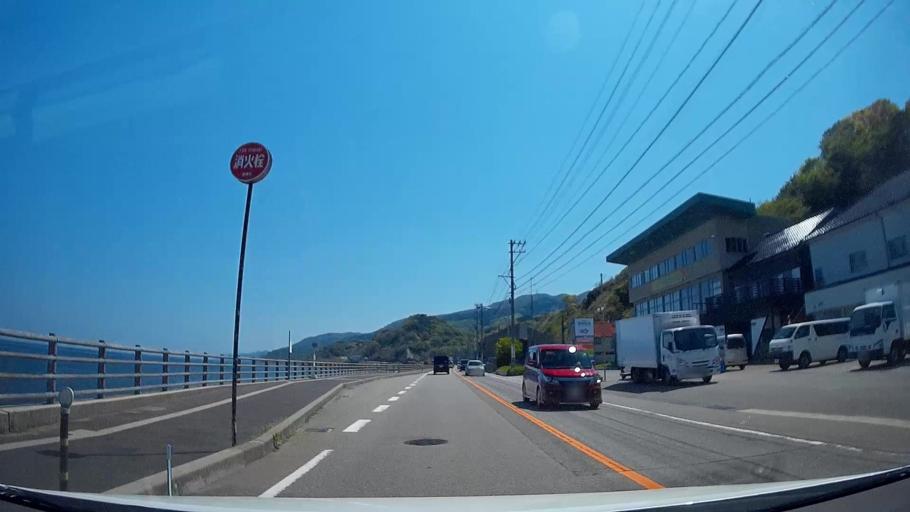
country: JP
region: Ishikawa
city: Nanao
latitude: 37.3946
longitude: 136.9199
